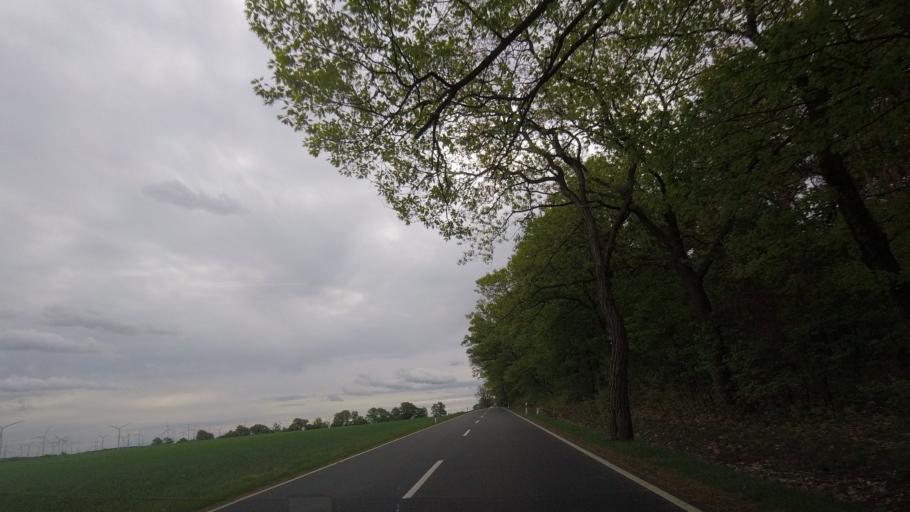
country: DE
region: Brandenburg
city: Dahme
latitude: 51.8534
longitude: 13.4981
